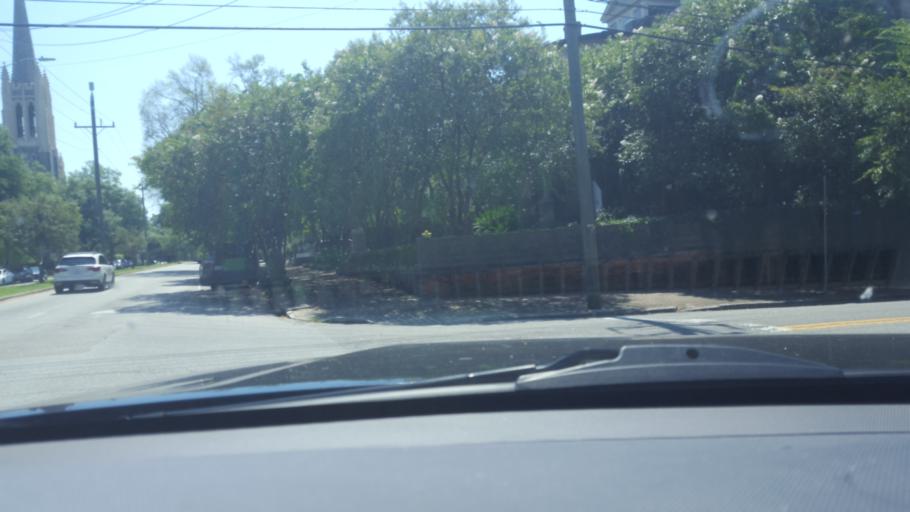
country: US
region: North Carolina
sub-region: New Hanover County
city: Wilmington
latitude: 34.2344
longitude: -77.9461
